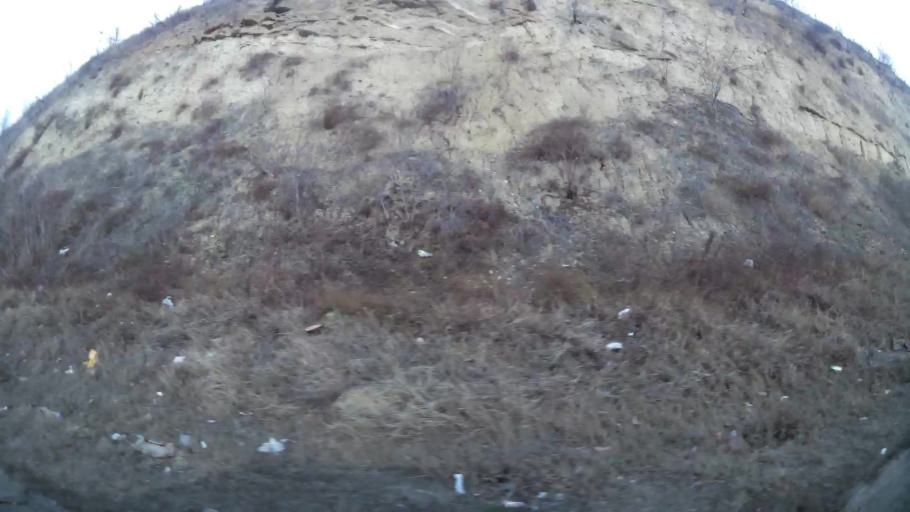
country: MK
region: Karpos
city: Skopje
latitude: 42.0142
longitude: 21.4155
